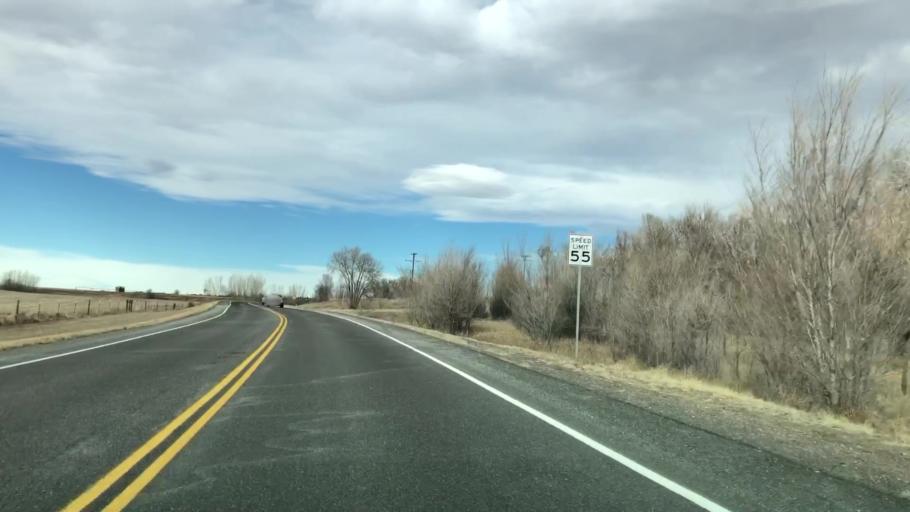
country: US
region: Colorado
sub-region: Weld County
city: Windsor
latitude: 40.5092
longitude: -104.9267
